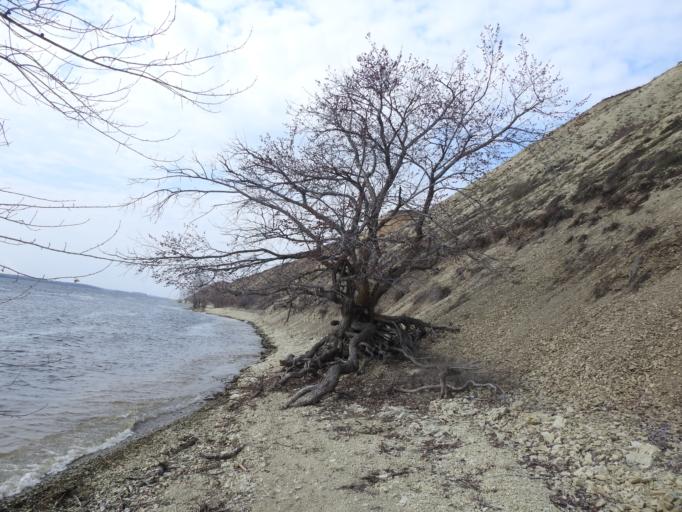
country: RU
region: Saratov
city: Voskresenskoye
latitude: 51.8050
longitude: 46.9126
